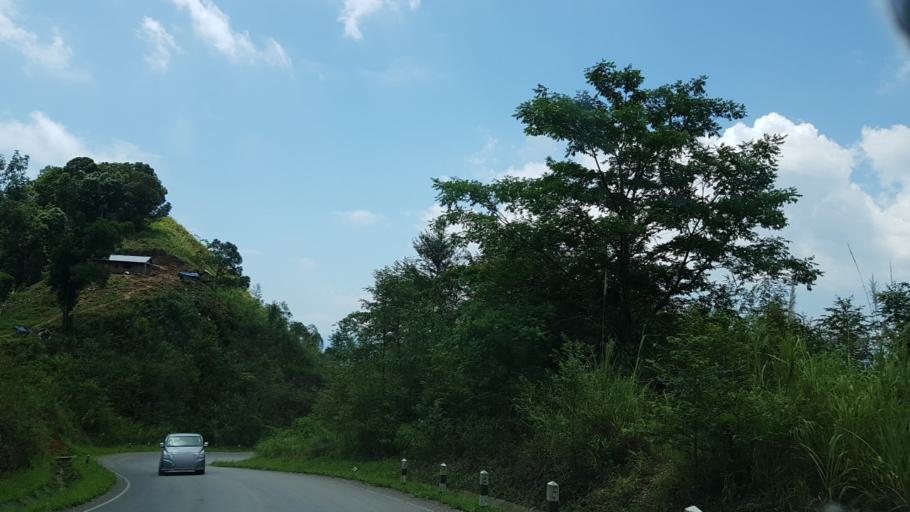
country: LA
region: Vientiane
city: Muang Kasi
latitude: 19.3795
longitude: 102.1563
